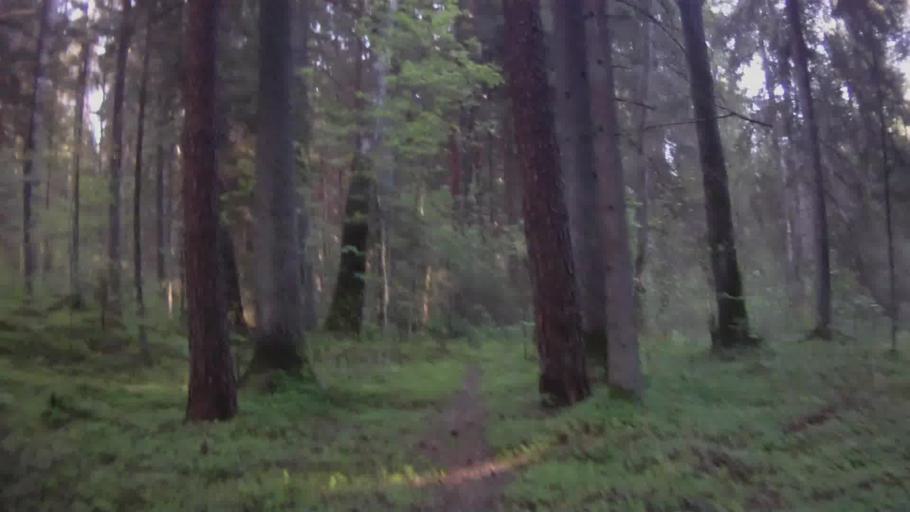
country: LV
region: Baldone
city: Baldone
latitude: 56.7474
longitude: 24.4196
